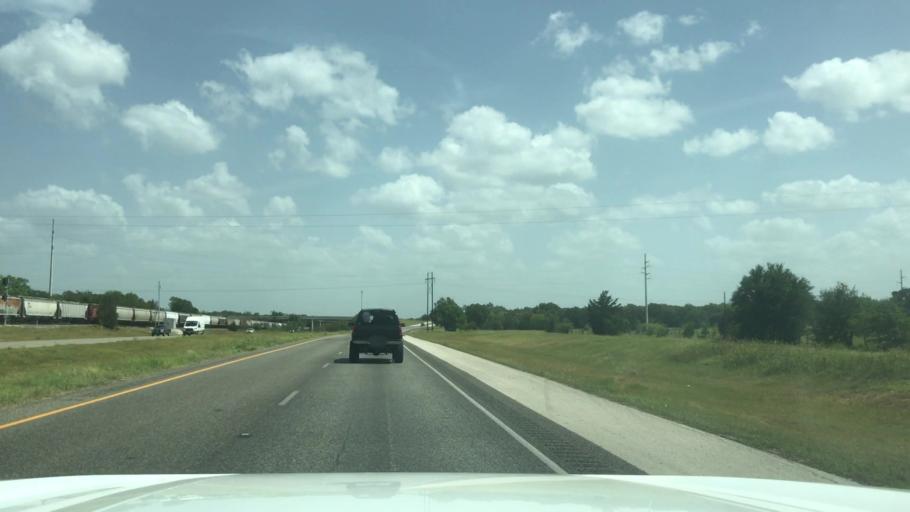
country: US
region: Texas
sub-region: Robertson County
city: Hearne
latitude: 30.9105
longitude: -96.6134
